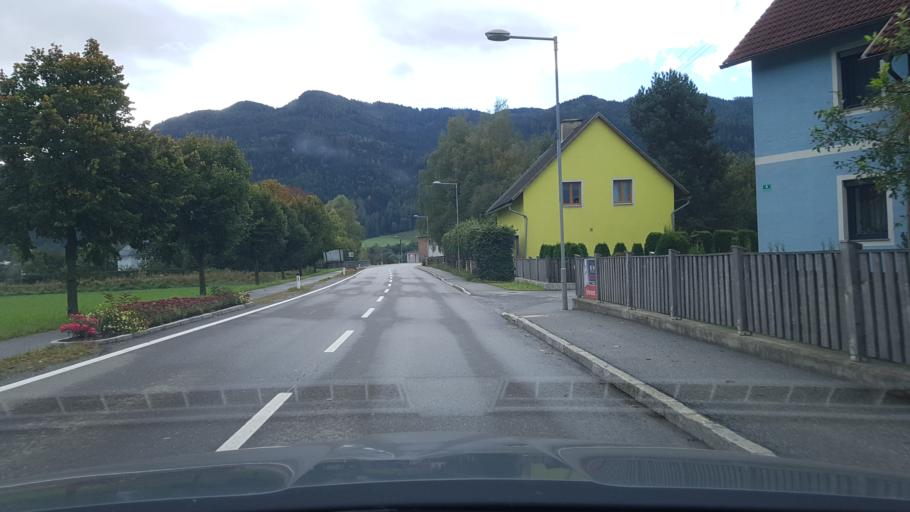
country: AT
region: Styria
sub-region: Politischer Bezirk Murau
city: Triebendorf
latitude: 47.1415
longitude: 14.2840
